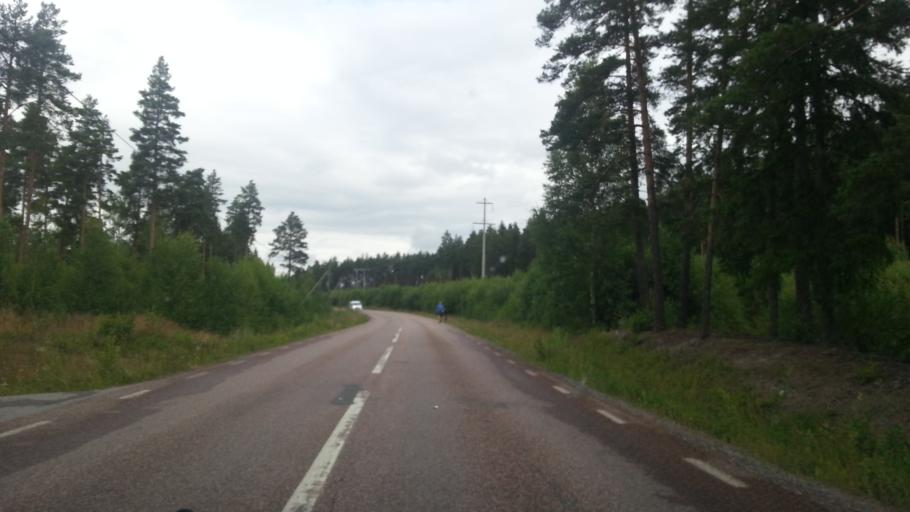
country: SE
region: Dalarna
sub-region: Faluns Kommun
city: Falun
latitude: 60.6482
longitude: 15.7854
